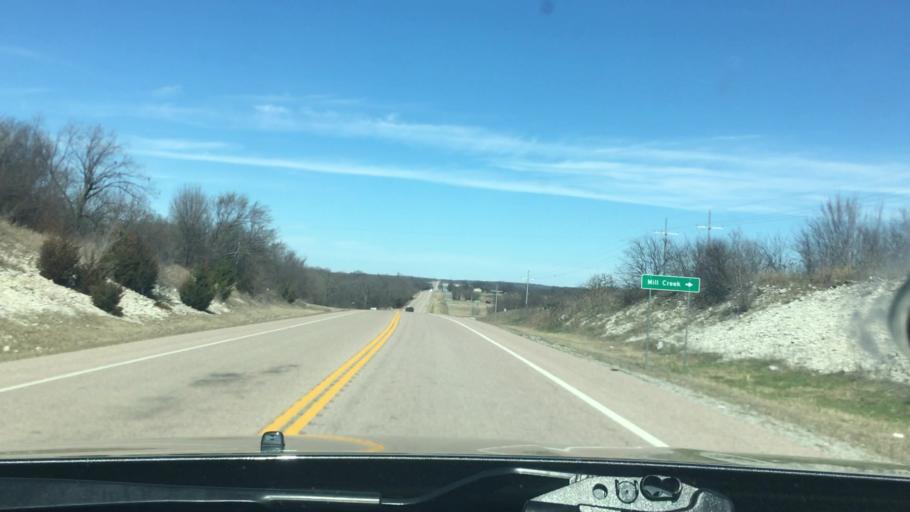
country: US
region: Oklahoma
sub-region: Murray County
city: Sulphur
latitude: 34.4060
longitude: -96.9507
